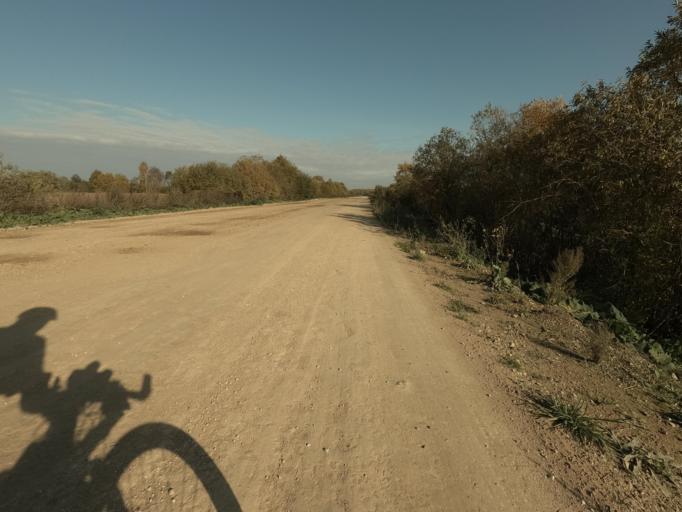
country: RU
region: Novgorod
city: Batetskiy
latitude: 58.8155
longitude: 30.6988
